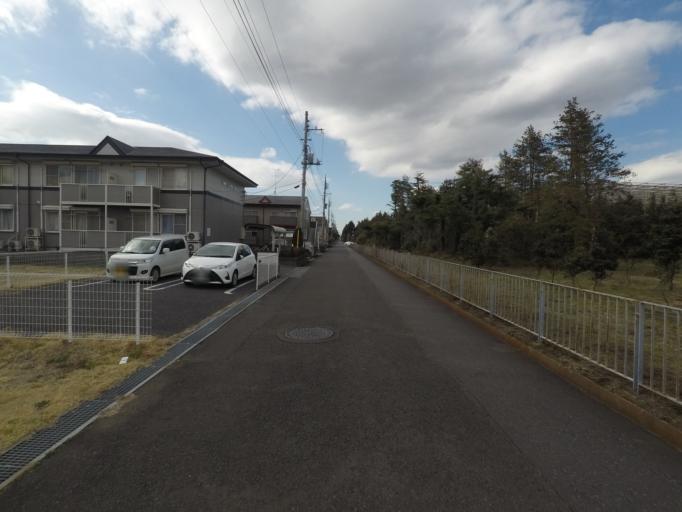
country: JP
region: Ibaraki
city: Ushiku
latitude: 36.0255
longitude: 140.0996
